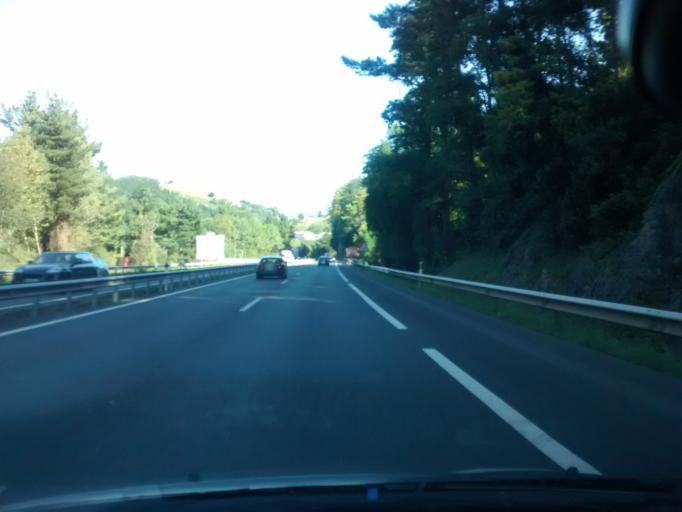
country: ES
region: Basque Country
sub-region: Provincia de Guipuzcoa
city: Deba
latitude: 43.2825
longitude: -2.3189
